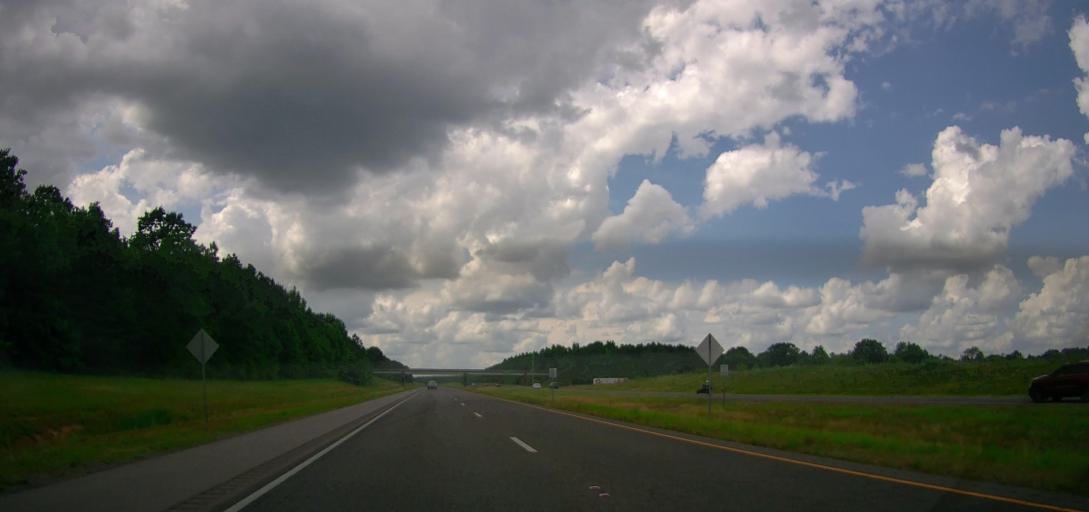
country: US
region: Alabama
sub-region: Walker County
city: Carbon Hill
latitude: 33.8867
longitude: -87.4515
